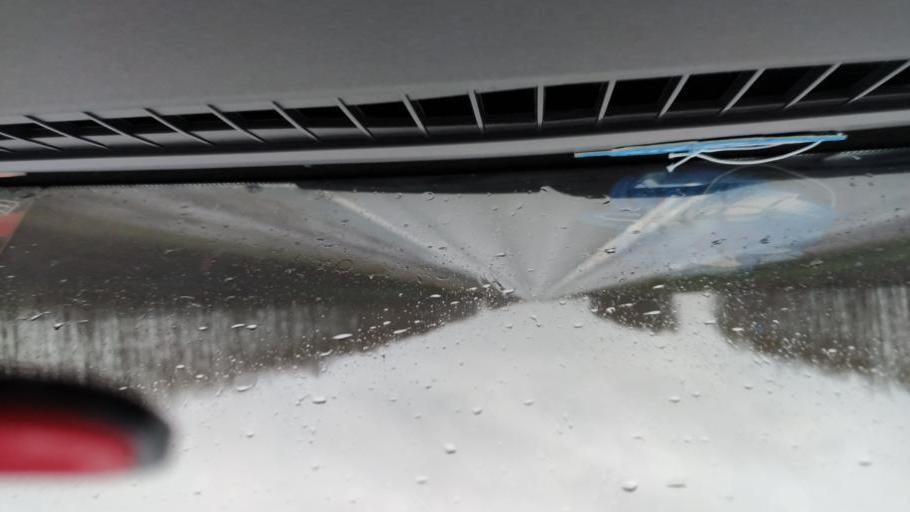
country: RU
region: Tatarstan
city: Mendeleyevsk
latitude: 55.9276
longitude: 52.2790
